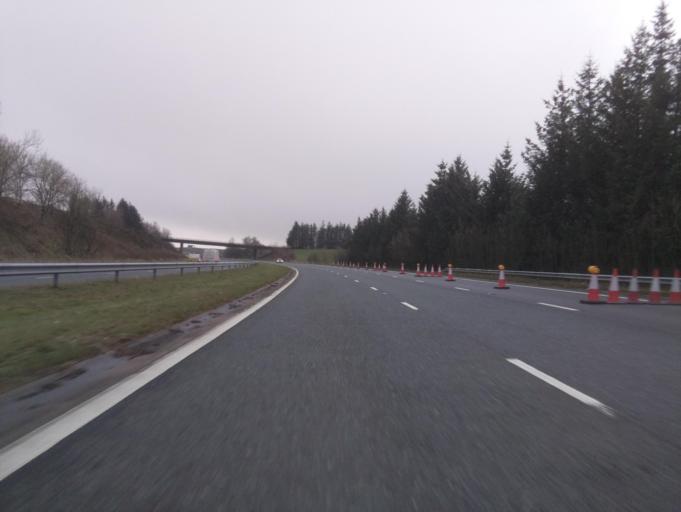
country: GB
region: England
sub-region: Cumbria
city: Sedbergh
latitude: 54.3553
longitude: -2.6186
